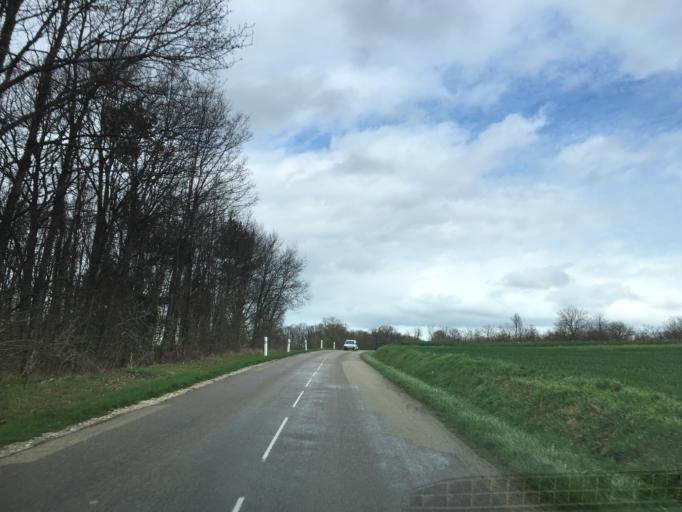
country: FR
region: Bourgogne
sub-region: Departement de l'Yonne
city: Charbuy
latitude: 47.8148
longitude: 3.4495
